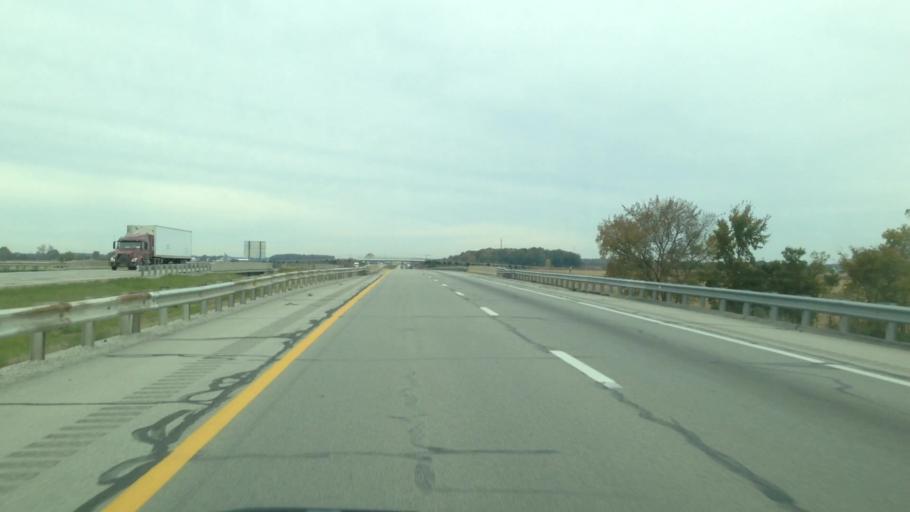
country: US
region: Ohio
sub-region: Williams County
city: West Unity
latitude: 41.6053
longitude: -84.4283
